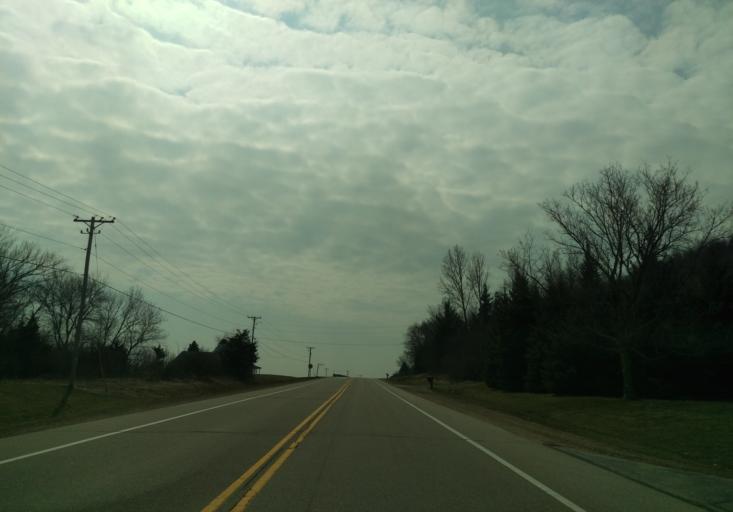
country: US
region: Wisconsin
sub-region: Columbia County
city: Lodi
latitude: 43.2925
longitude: -89.5219
